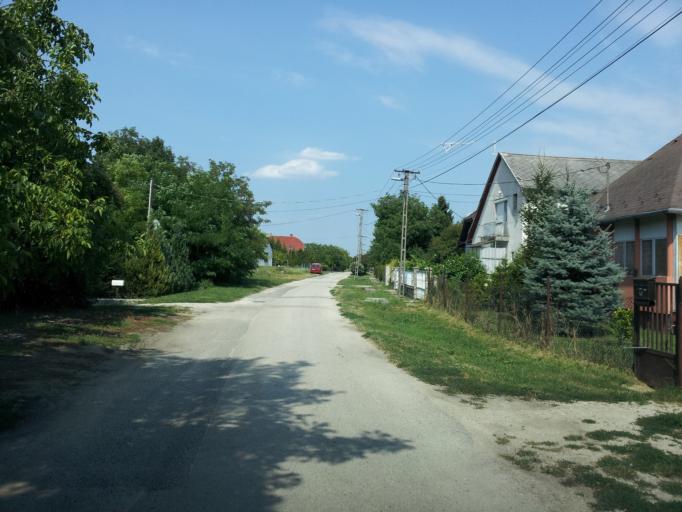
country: HU
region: Veszprem
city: Balatonkenese
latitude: 47.0799
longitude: 18.0811
